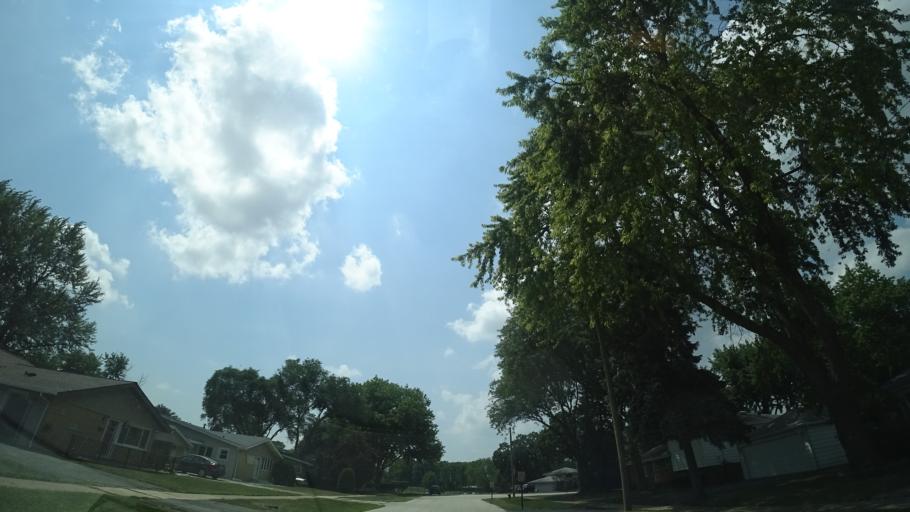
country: US
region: Illinois
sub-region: Cook County
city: Worth
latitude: 41.6950
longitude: -87.7924
